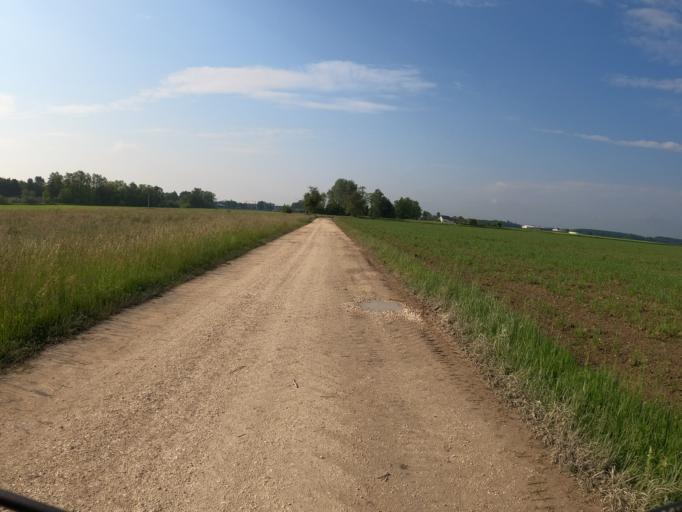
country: DE
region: Bavaria
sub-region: Swabia
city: Pfaffenhofen an der Roth
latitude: 48.3902
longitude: 10.1422
